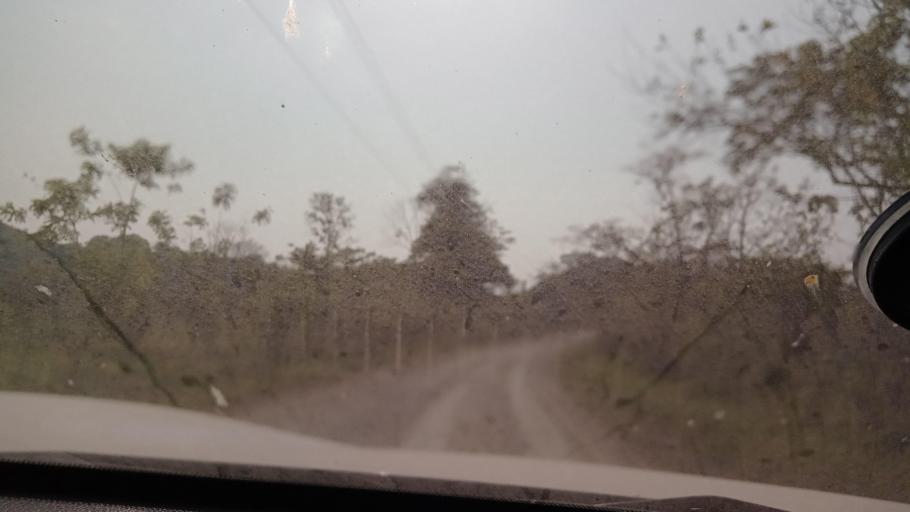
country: MX
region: Tabasco
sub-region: Huimanguillo
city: Francisco Rueda
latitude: 17.6121
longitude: -93.9359
